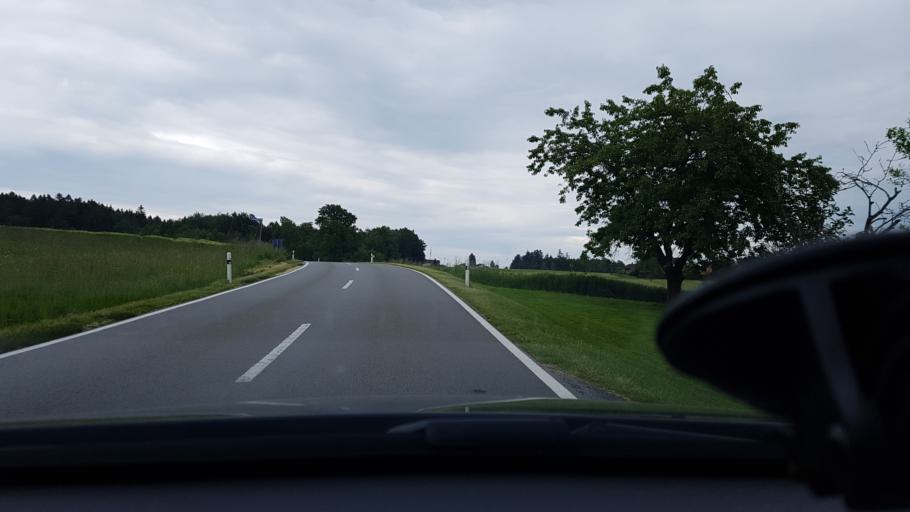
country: DE
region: Bavaria
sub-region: Lower Bavaria
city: Stubenberg
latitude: 48.3398
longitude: 13.0431
